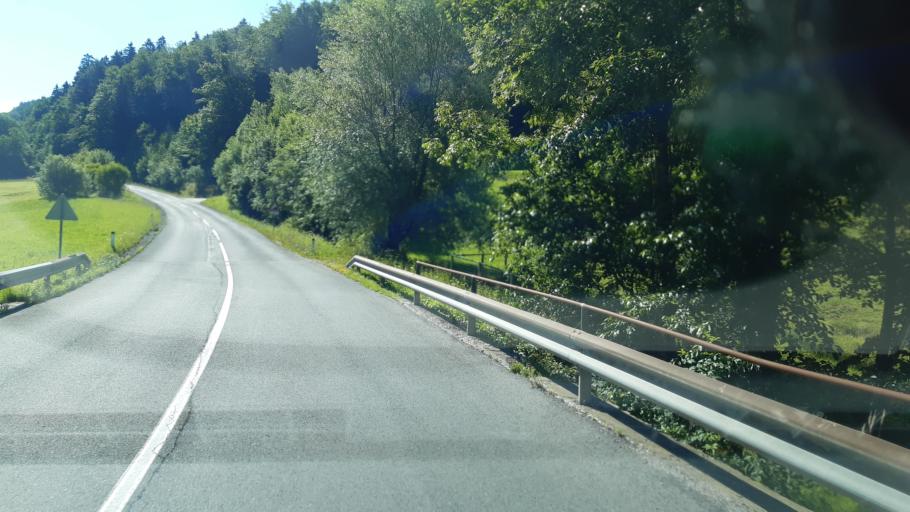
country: SI
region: Gornji Grad
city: Gornji Grad
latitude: 46.2165
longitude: 14.7936
